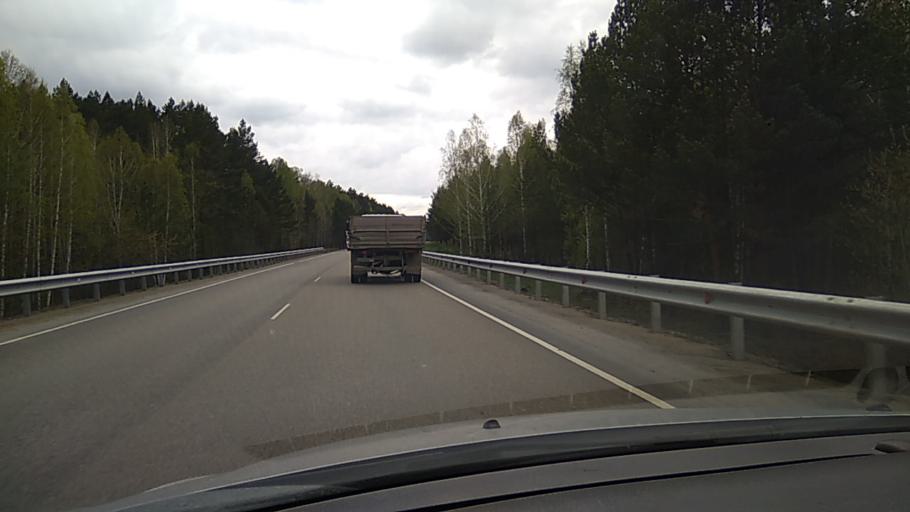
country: RU
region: Kurgan
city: Kataysk
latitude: 56.2983
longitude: 62.3831
